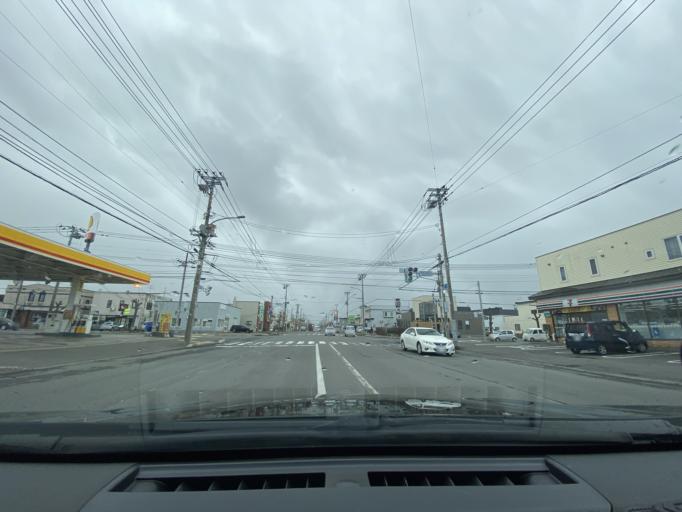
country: JP
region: Hokkaido
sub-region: Asahikawa-shi
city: Asahikawa
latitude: 43.8117
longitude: 142.3774
